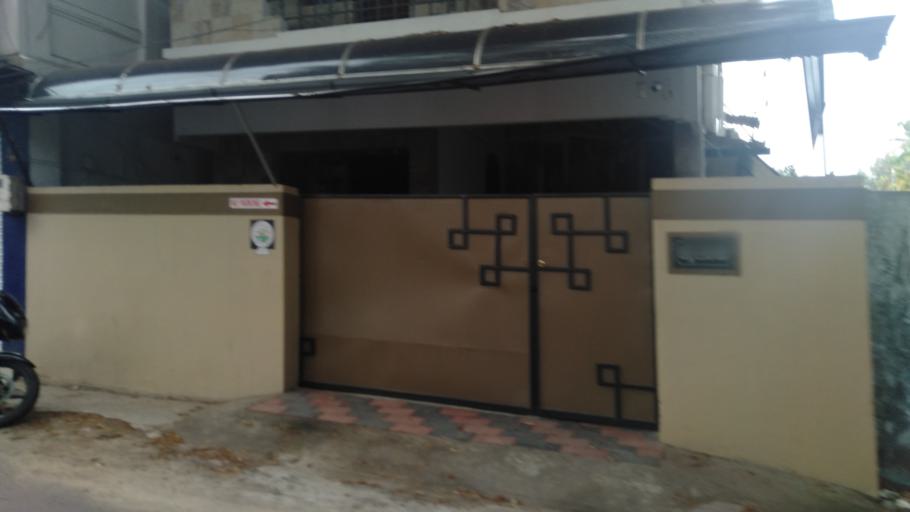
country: IN
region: Kerala
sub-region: Alappuzha
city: Alleppey
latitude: 9.4942
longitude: 76.3246
